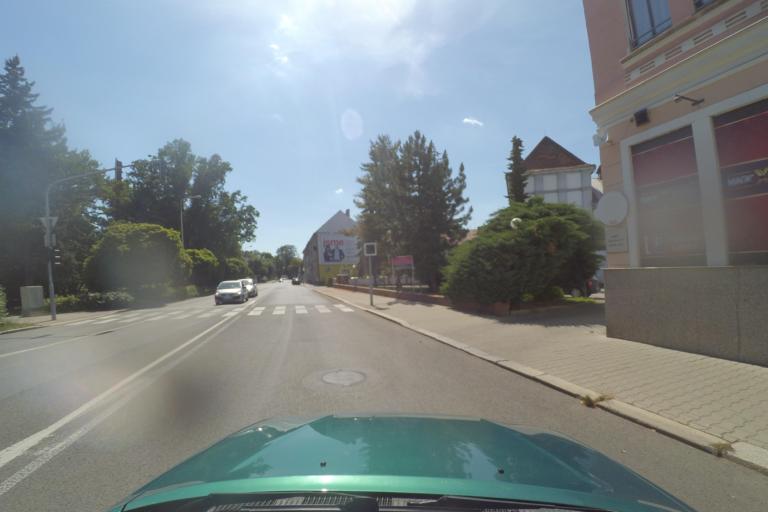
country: CZ
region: Liberecky
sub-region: Okres Ceska Lipa
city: Ceska Lipa
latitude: 50.6797
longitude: 14.5365
